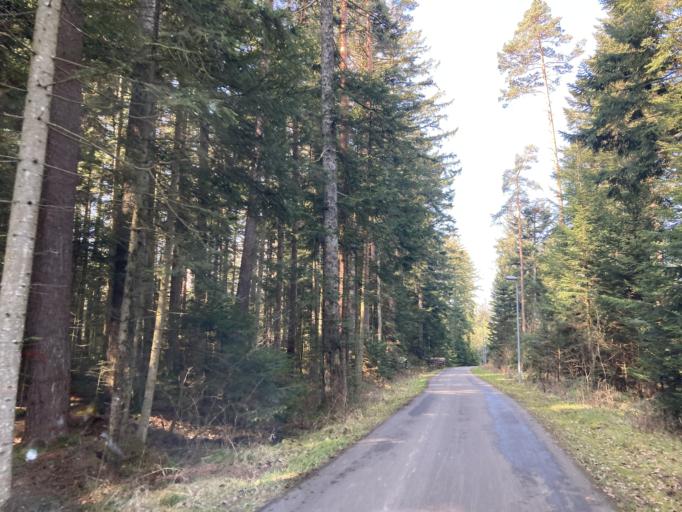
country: DE
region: Baden-Wuerttemberg
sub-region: Karlsruhe Region
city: Schomberg
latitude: 48.7800
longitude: 8.6392
